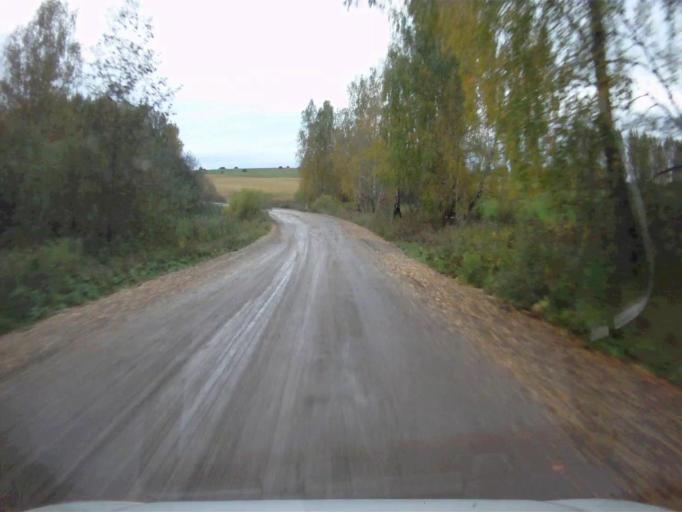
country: RU
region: Sverdlovsk
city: Mikhaylovsk
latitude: 56.1752
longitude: 59.2157
